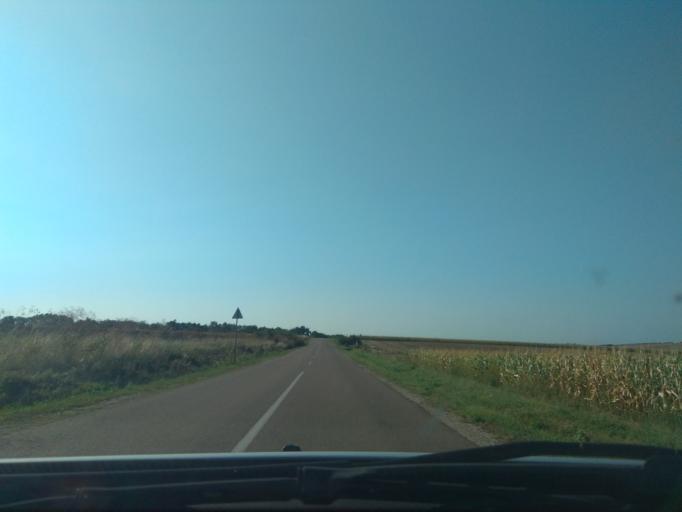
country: HU
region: Borsod-Abauj-Zemplen
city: Emod
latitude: 47.9654
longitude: 20.8011
